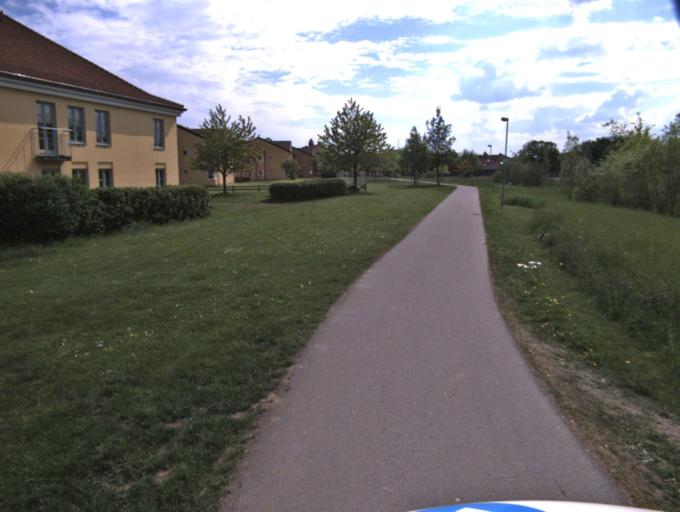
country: SE
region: Skane
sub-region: Kristianstads Kommun
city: Kristianstad
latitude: 56.0510
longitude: 14.1483
